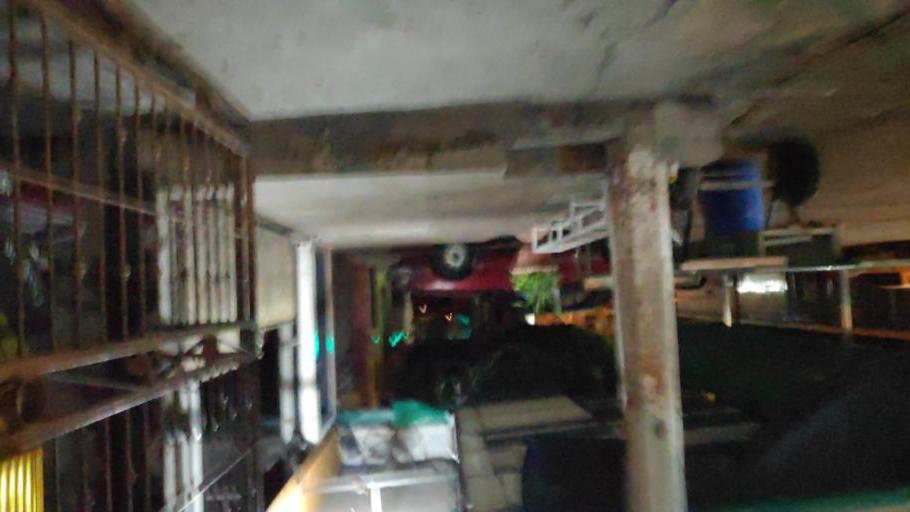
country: MX
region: Sinaloa
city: Culiacan
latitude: 24.8013
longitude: -107.3997
